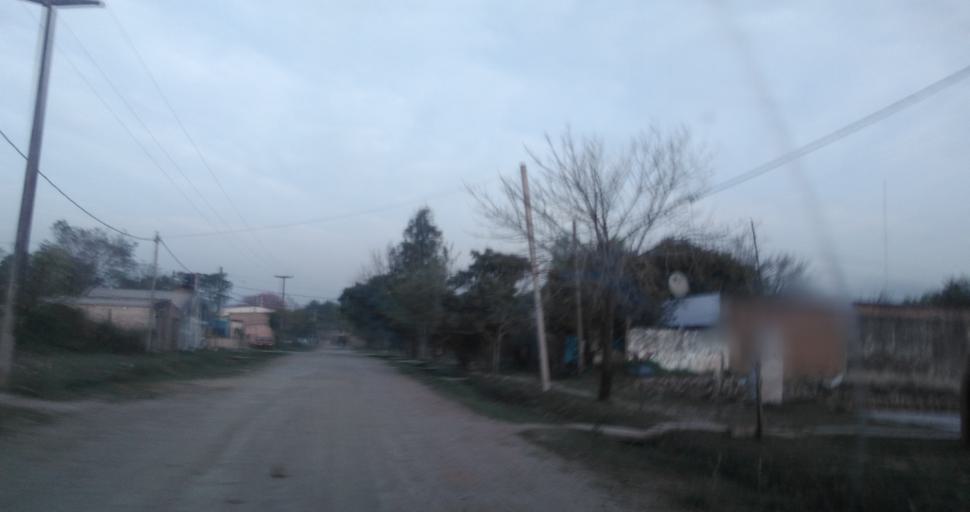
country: AR
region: Chaco
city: Resistencia
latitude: -27.4721
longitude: -59.0129
